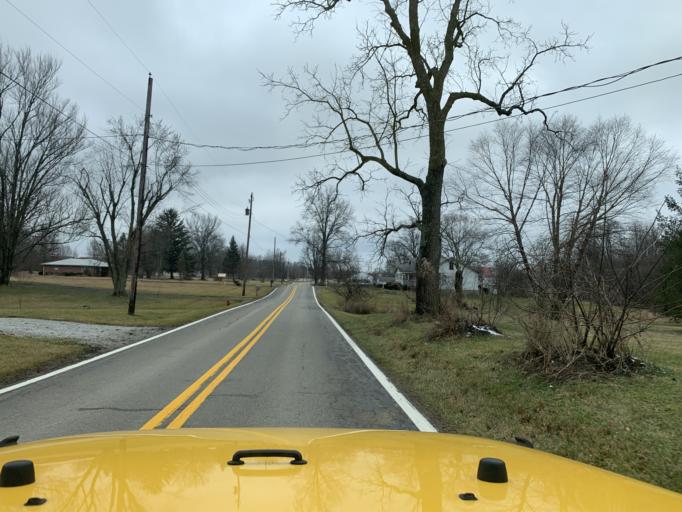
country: US
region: Ohio
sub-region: Franklin County
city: New Albany
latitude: 40.0951
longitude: -82.7931
